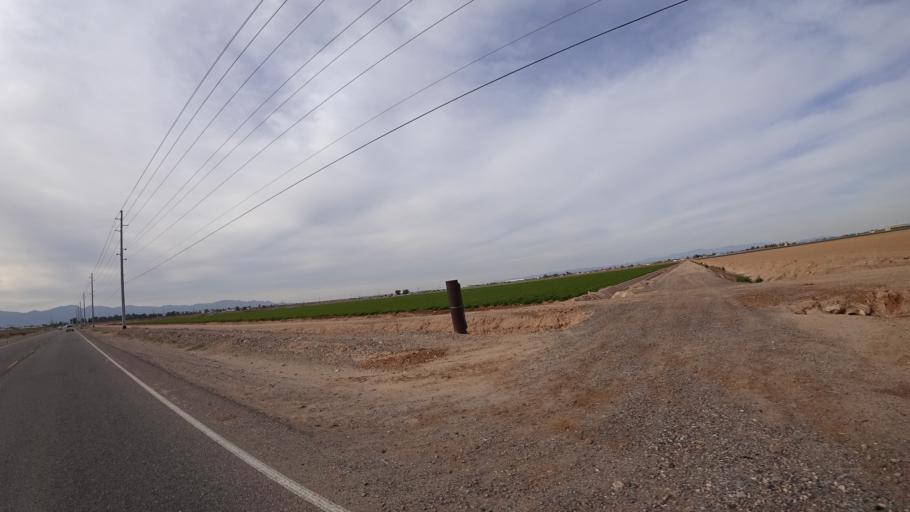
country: US
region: Arizona
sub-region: Maricopa County
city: Youngtown
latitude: 33.5655
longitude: -112.3329
